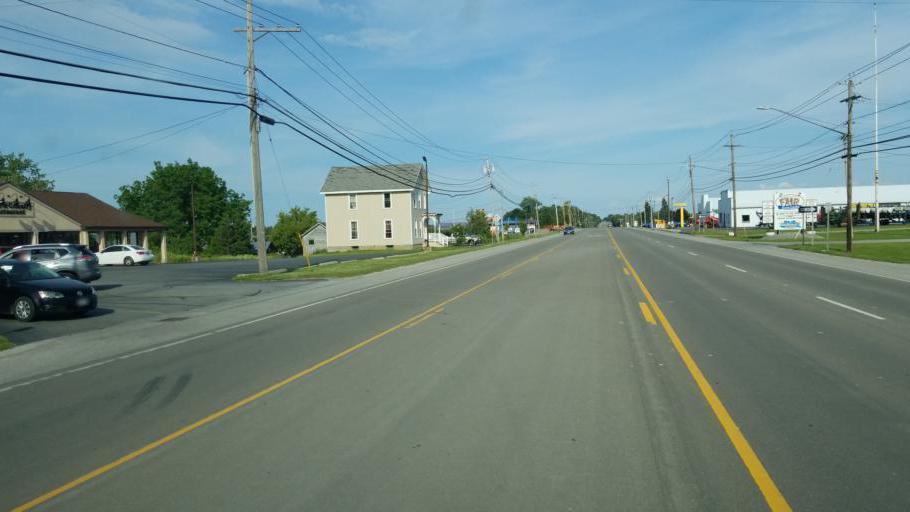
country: US
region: New York
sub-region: Genesee County
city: Batavia
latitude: 42.9924
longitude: -78.1484
